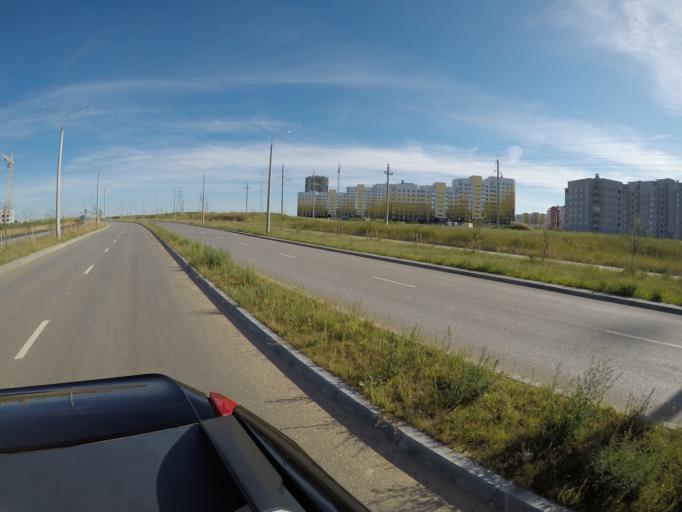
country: BY
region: Grodnenskaya
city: Hrodna
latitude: 53.7216
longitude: 23.8686
